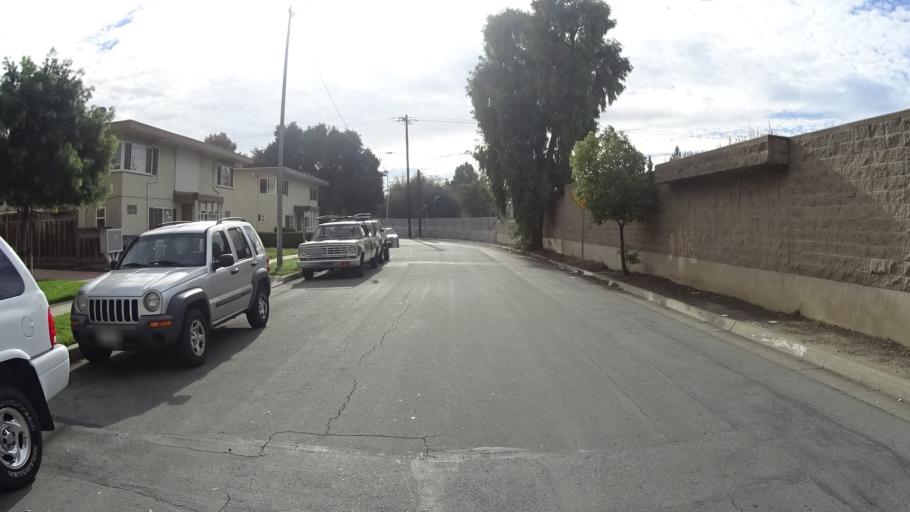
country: US
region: California
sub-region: Santa Clara County
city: Burbank
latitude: 37.3352
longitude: -121.9350
